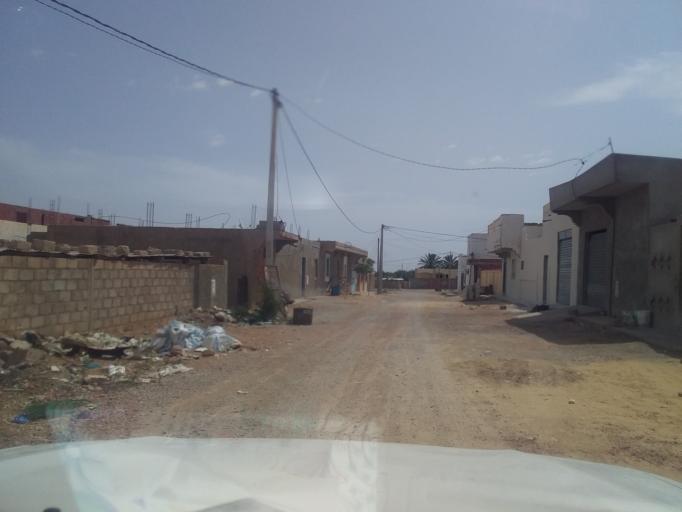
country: TN
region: Madanin
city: Medenine
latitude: 33.5870
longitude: 10.3230
